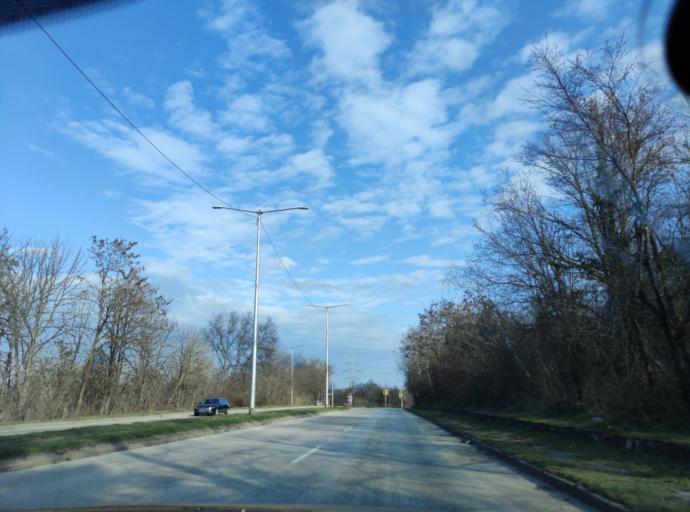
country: BG
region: Pleven
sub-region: Obshtina Pleven
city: Pleven
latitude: 43.4345
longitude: 24.5708
